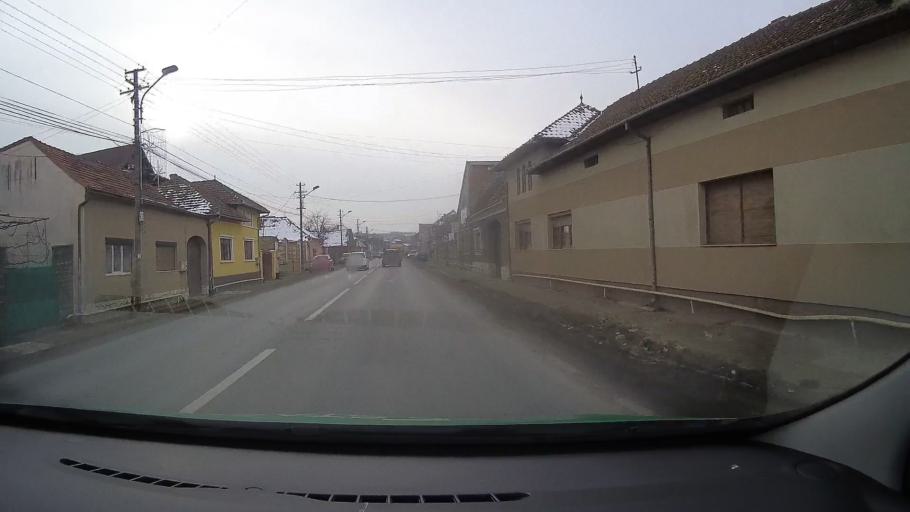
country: RO
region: Hunedoara
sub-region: Municipiul Orastie
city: Orastie
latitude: 45.8459
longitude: 23.2041
